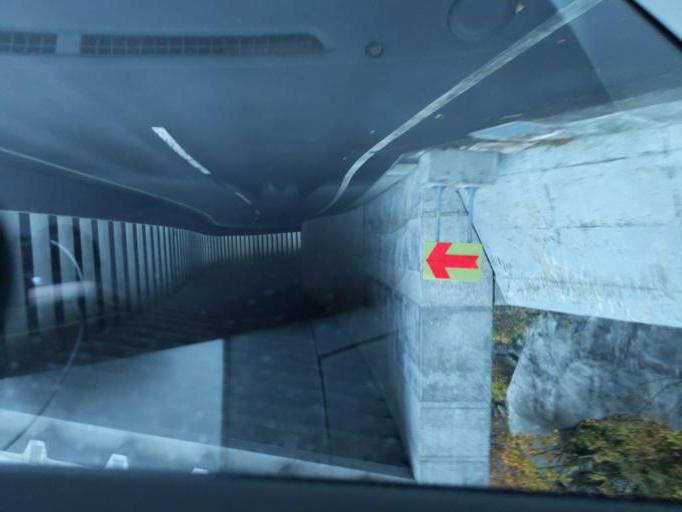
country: JP
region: Iwate
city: Mizusawa
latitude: 39.1127
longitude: 140.8463
